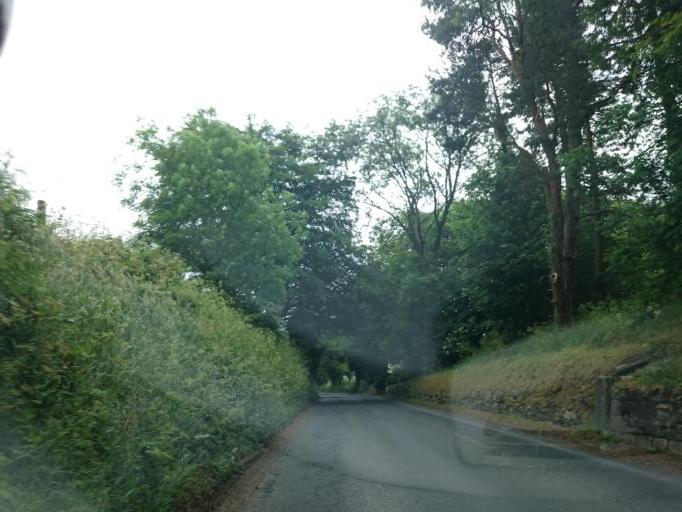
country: IE
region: Leinster
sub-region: Wicklow
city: Carnew
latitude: 52.8199
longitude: -6.5086
